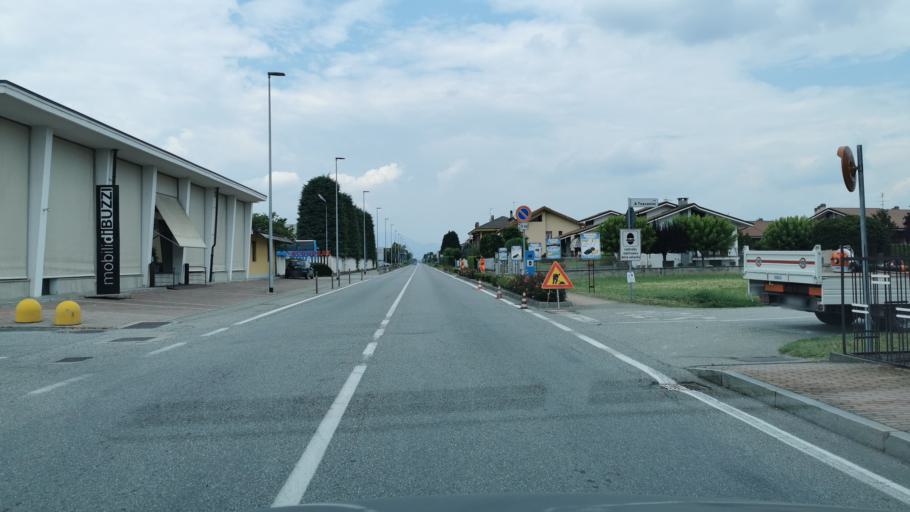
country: IT
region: Piedmont
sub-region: Provincia di Torino
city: Cavour
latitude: 44.7928
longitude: 7.3750
